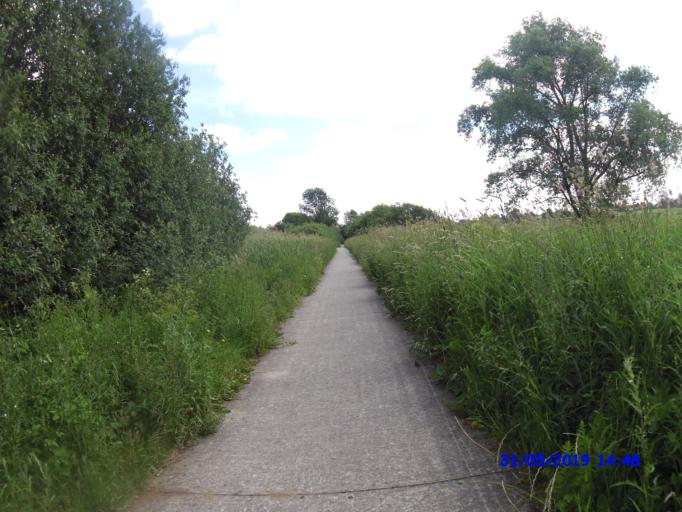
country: FR
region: Nord-Pas-de-Calais
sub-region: Departement du Nord
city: Deulemont
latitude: 50.7944
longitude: 2.9578
